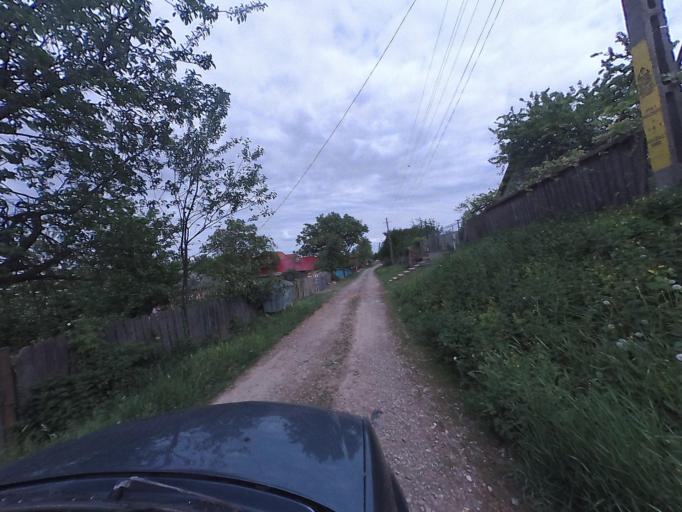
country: RO
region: Neamt
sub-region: Comuna Dulcesti
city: Dulcesti
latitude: 46.9612
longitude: 26.7816
